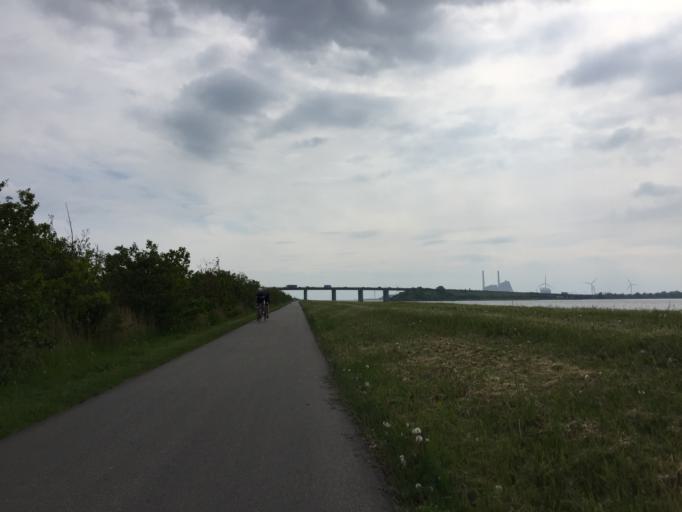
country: DK
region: Capital Region
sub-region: Hvidovre Kommune
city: Hvidovre
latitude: 55.6196
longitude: 12.5207
